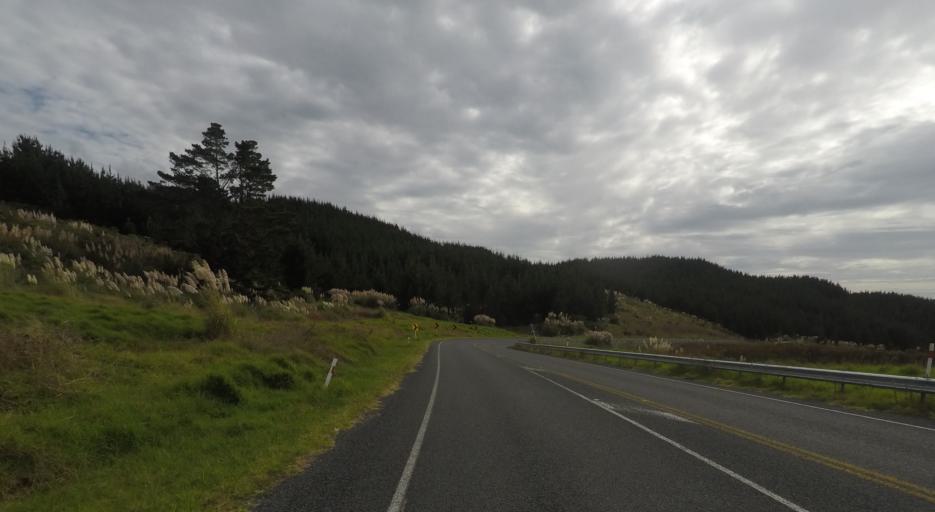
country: NZ
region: Auckland
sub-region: Auckland
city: Rothesay Bay
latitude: -36.6558
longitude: 174.6996
